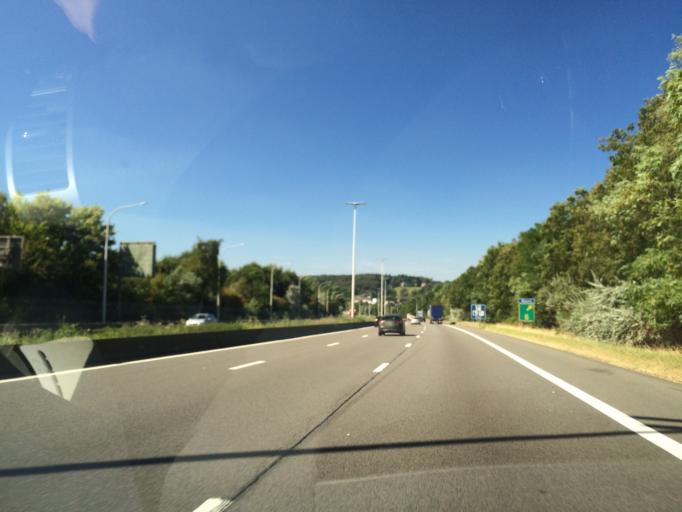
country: BE
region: Wallonia
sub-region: Province du Brabant Wallon
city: Wavre
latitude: 50.7042
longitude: 4.6123
